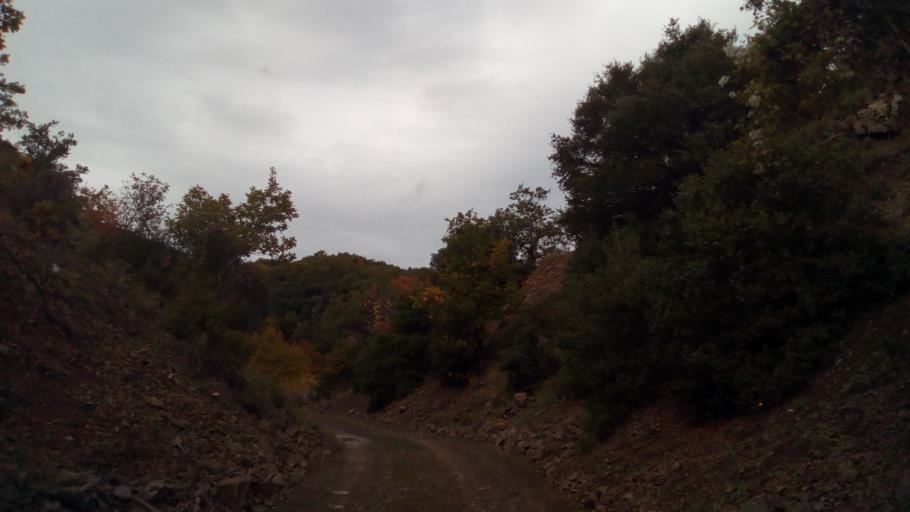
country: GR
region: West Greece
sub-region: Nomos Aitolias kai Akarnanias
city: Nafpaktos
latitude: 38.5533
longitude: 21.9681
